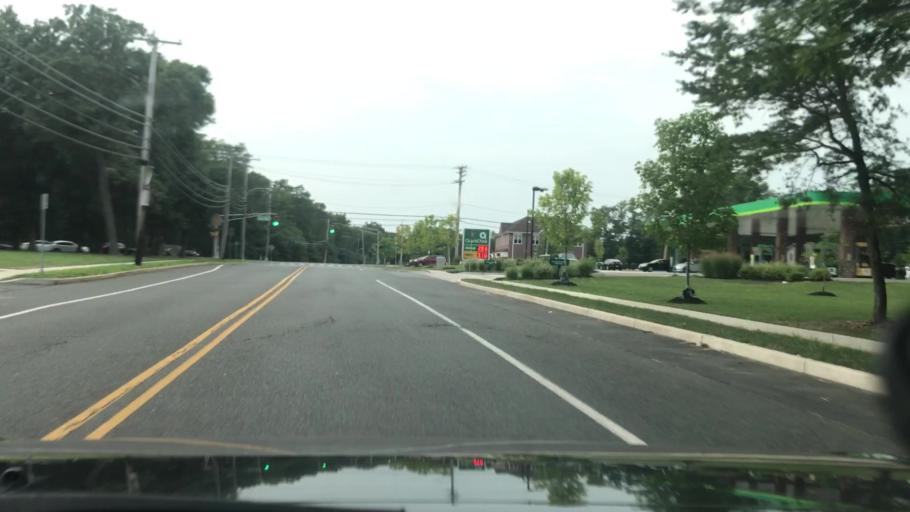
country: US
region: New Jersey
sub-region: Ocean County
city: Lakewood
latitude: 40.1260
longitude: -74.2544
